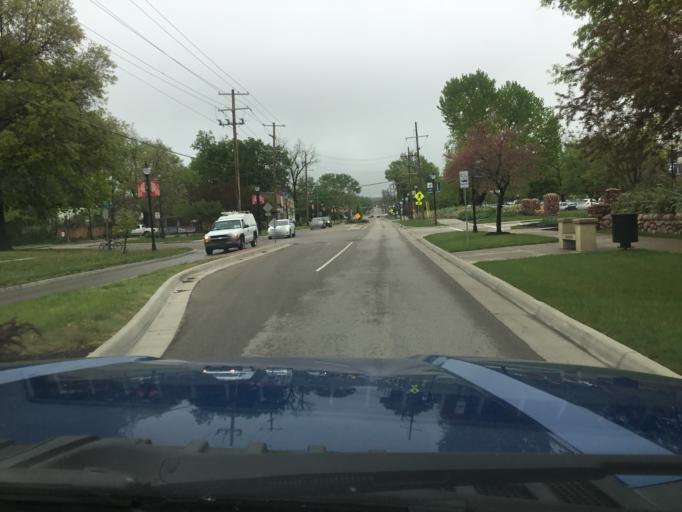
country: US
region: Kansas
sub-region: Shawnee County
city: Topeka
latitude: 39.0369
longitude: -95.7010
